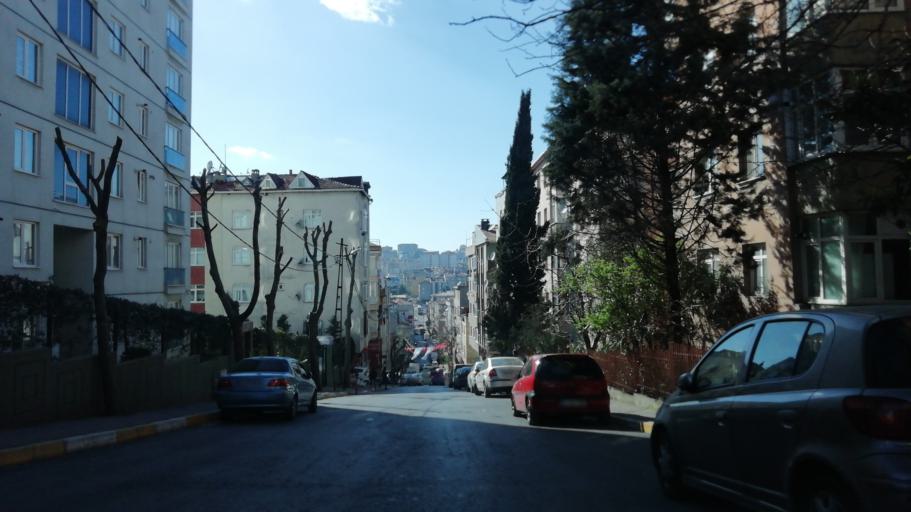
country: TR
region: Istanbul
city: Bagcilar
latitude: 41.0366
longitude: 28.8512
